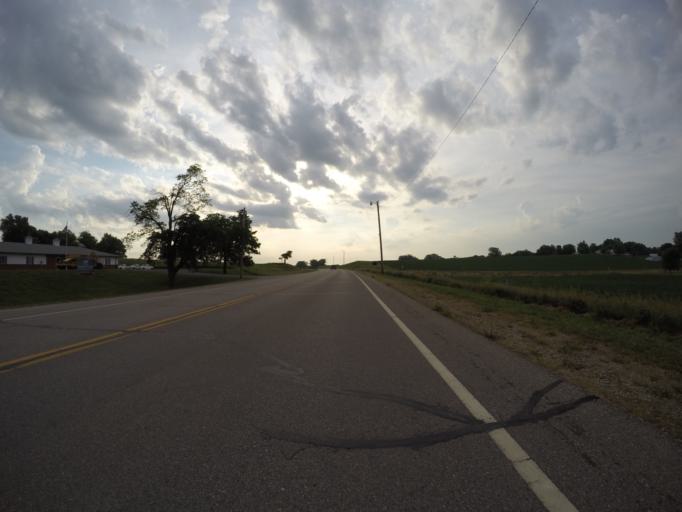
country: US
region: Kansas
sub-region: Doniphan County
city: Troy
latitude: 39.7899
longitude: -95.0842
